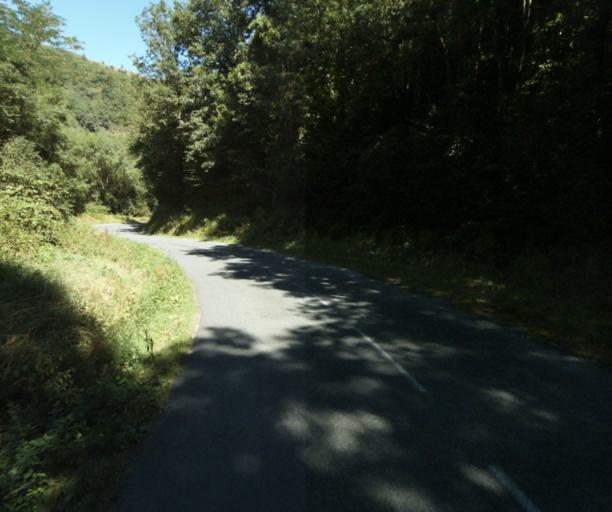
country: FR
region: Midi-Pyrenees
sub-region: Departement du Tarn
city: Soreze
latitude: 43.4409
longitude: 2.0849
